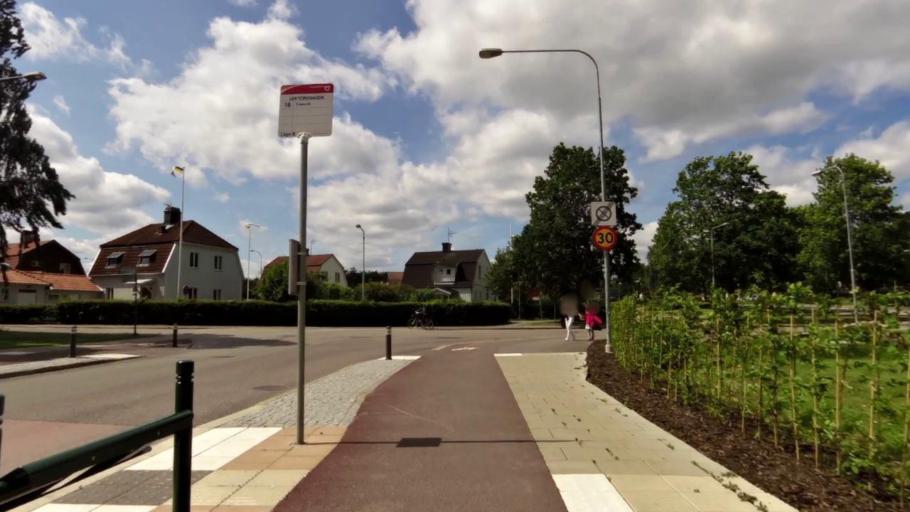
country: SE
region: OEstergoetland
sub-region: Linkopings Kommun
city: Linkoping
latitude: 58.4123
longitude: 15.5975
